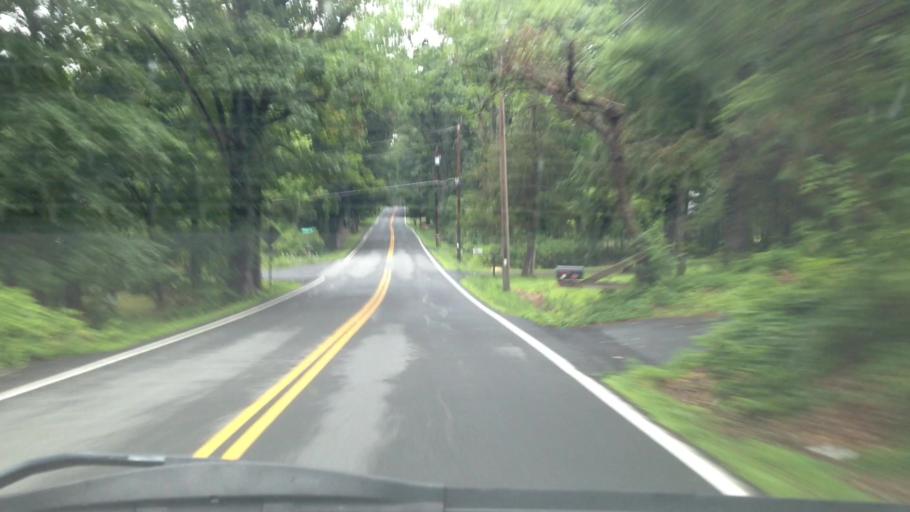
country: US
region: New York
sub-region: Ulster County
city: New Paltz
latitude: 41.7654
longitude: -74.0572
